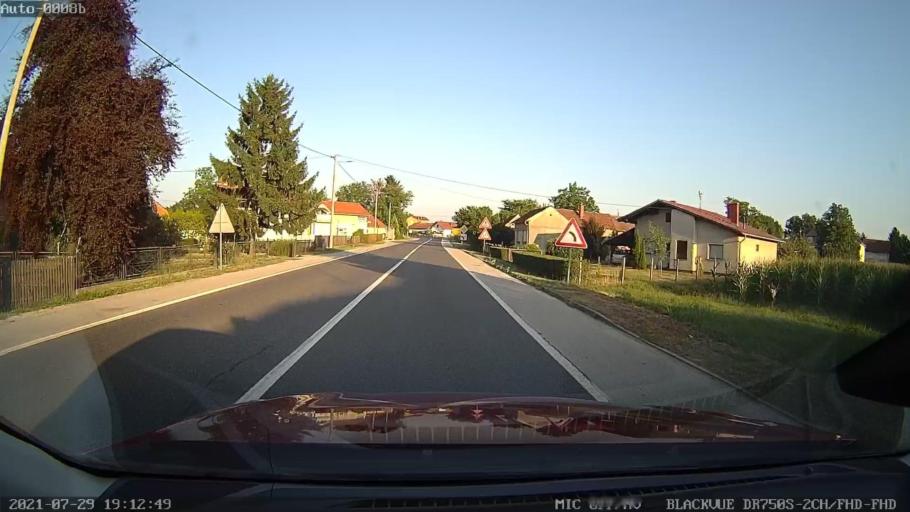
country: HR
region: Varazdinska
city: Jalzabet
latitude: 46.2648
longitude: 16.5189
